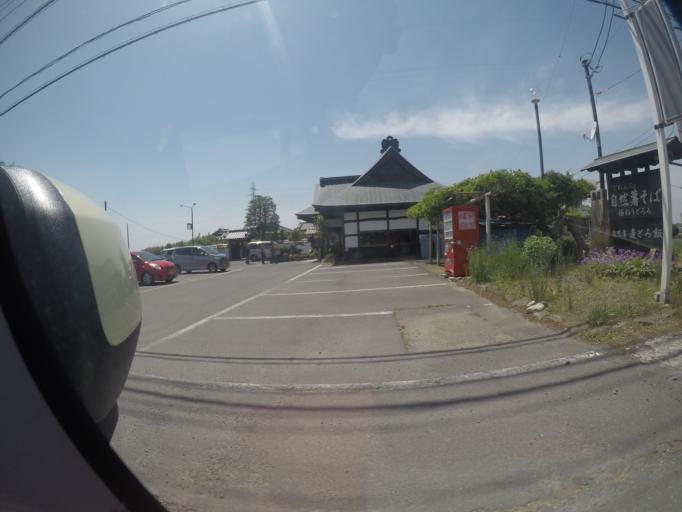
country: JP
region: Ibaraki
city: Tsukuba
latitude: 36.2101
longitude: 140.0718
